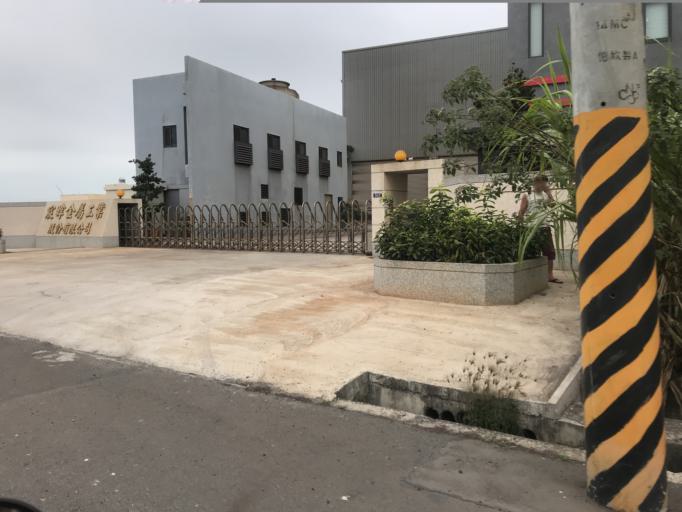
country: TW
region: Taiwan
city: Fengyuan
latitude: 24.3756
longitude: 120.5961
